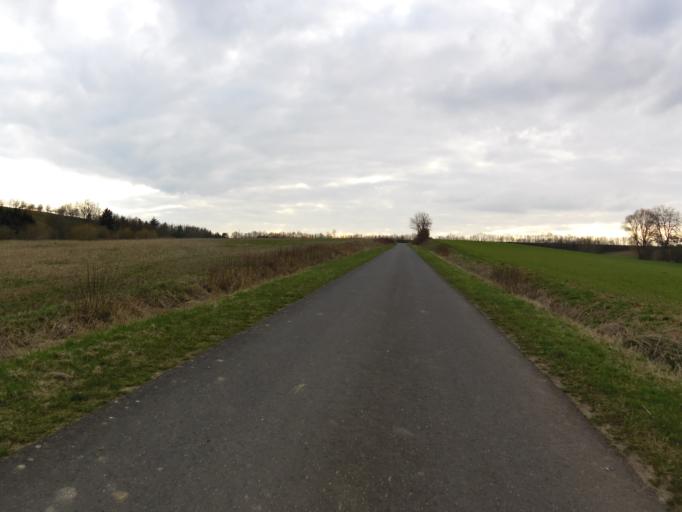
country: DE
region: Bavaria
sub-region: Regierungsbezirk Unterfranken
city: Buchbrunn
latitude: 49.7475
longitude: 10.1148
